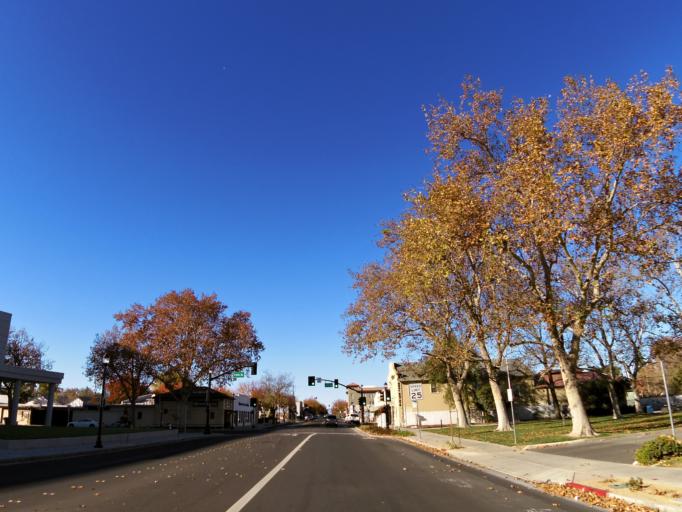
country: US
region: California
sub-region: Yolo County
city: Woodland
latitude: 38.6774
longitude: -121.7675
